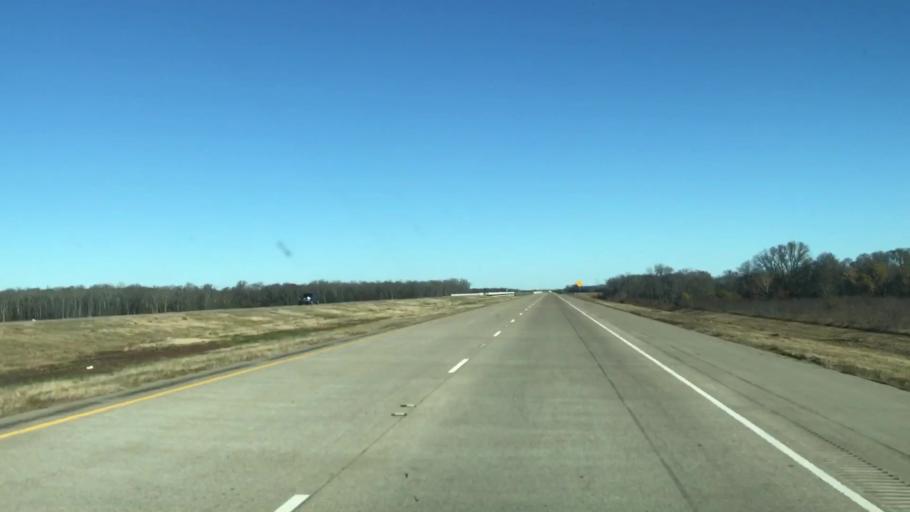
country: US
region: Louisiana
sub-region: Caddo Parish
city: Blanchard
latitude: 32.6202
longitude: -93.8355
